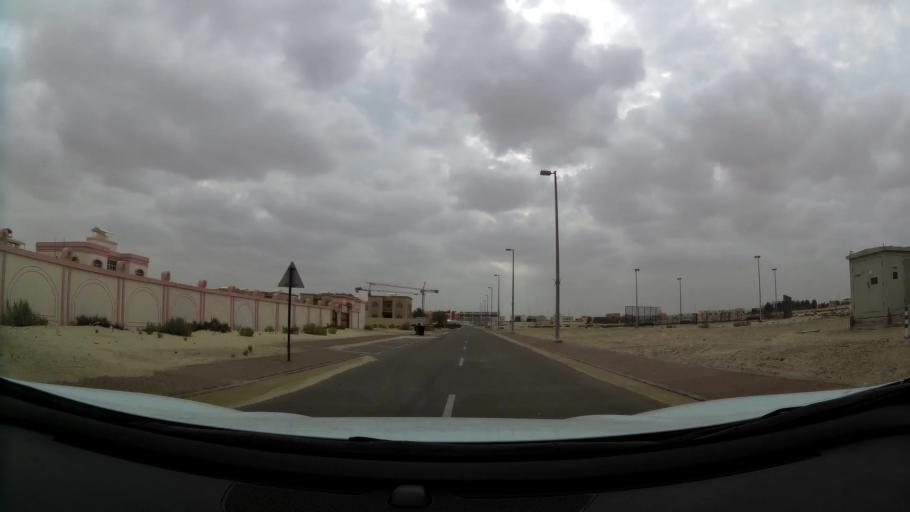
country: AE
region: Abu Dhabi
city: Abu Dhabi
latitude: 24.3748
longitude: 54.6412
